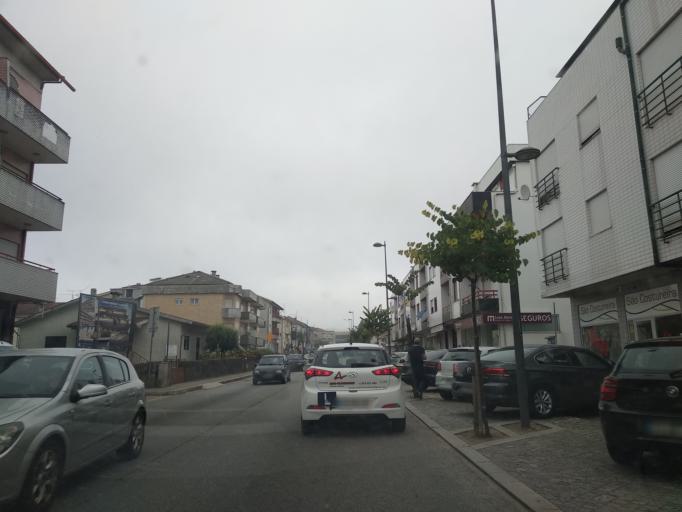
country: PT
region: Braga
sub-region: Vila Verde
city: Vila Verde
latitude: 41.6450
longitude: -8.4356
